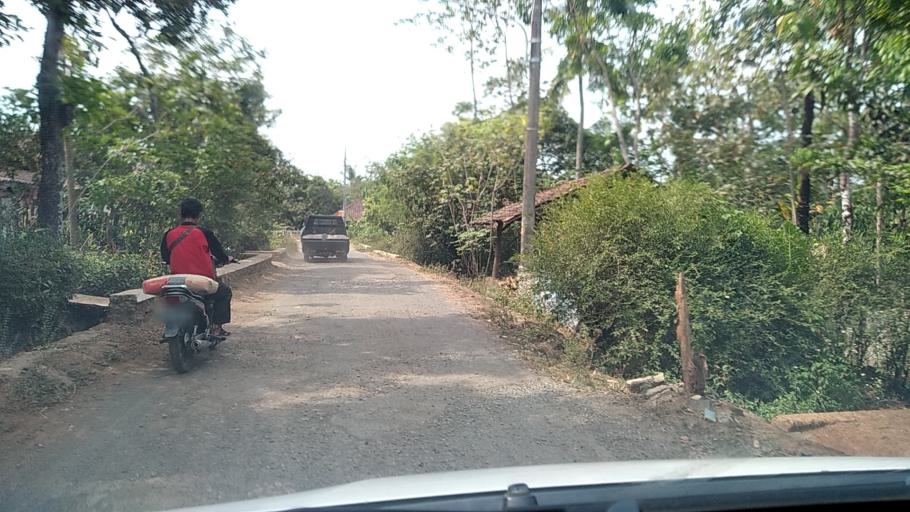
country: ID
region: Central Java
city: Ungaran
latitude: -7.0604
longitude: 110.3035
